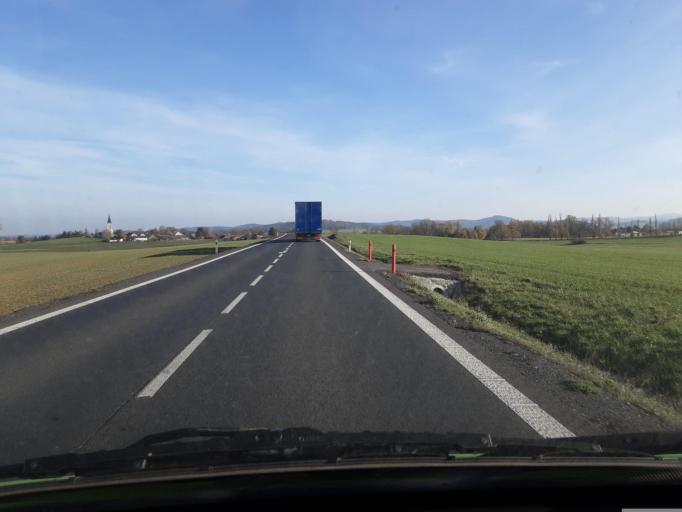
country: CZ
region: Plzensky
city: Hradek
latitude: 49.3270
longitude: 13.5855
